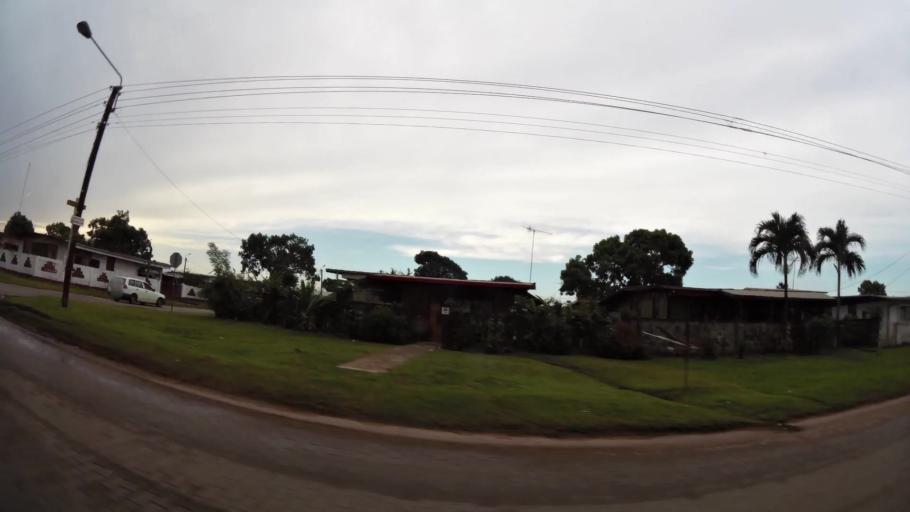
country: SR
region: Paramaribo
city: Paramaribo
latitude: 5.8050
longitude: -55.1999
